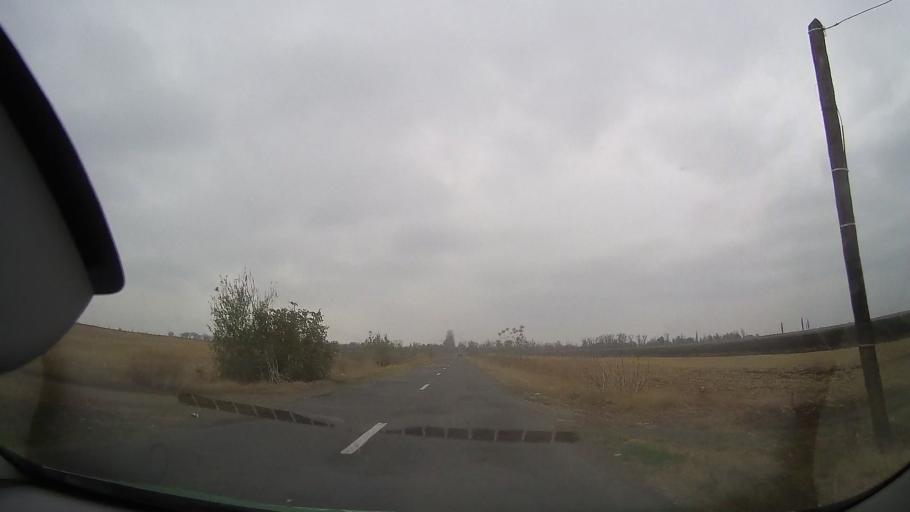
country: RO
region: Ialomita
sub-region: Comuna Garbovi
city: Garbovi
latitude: 44.7679
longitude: 26.7909
